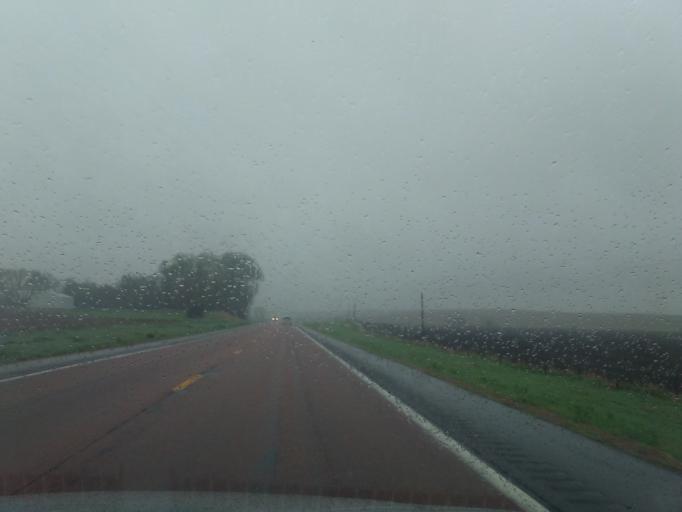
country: US
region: Nebraska
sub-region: Wayne County
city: Wayne
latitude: 42.2357
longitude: -97.1042
